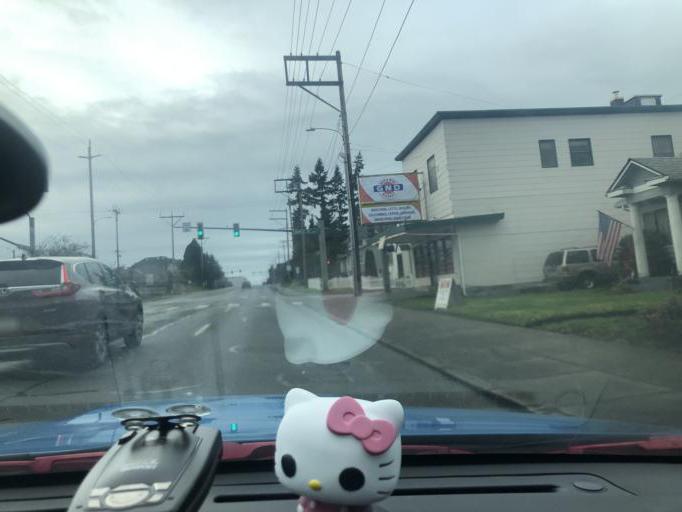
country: US
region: Washington
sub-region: Snohomish County
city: Everett
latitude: 47.9818
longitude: -122.1903
